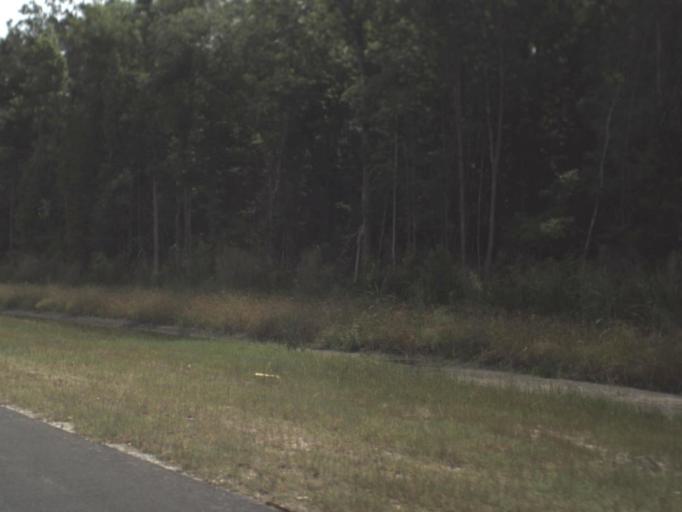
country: US
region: Florida
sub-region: Nassau County
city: Callahan
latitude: 30.5381
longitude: -81.8537
